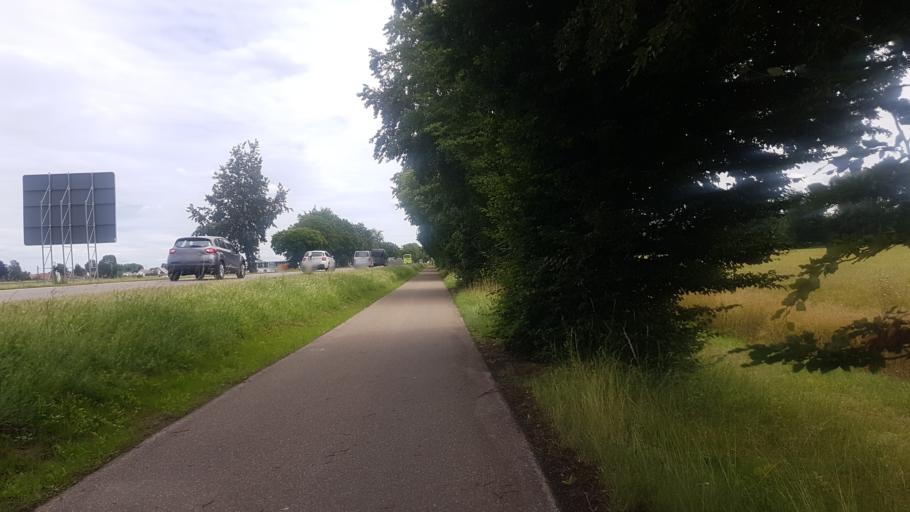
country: DE
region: Bavaria
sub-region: Swabia
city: Lauingen
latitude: 48.5756
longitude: 10.4587
